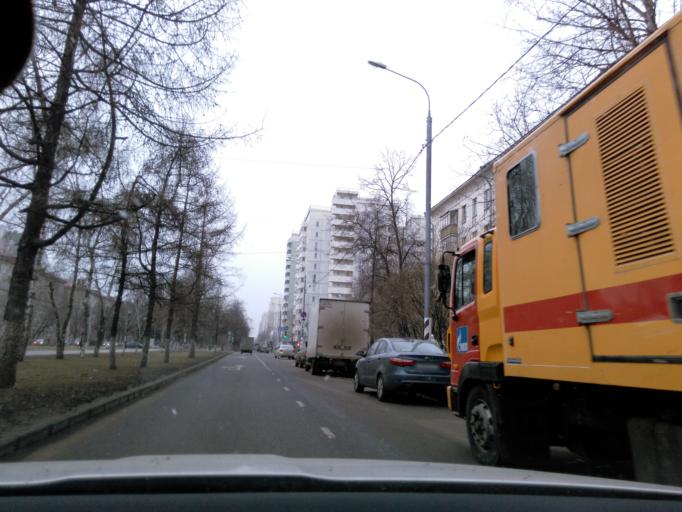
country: RU
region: Moscow
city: Novyye Cheremushki
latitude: 55.6895
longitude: 37.5870
